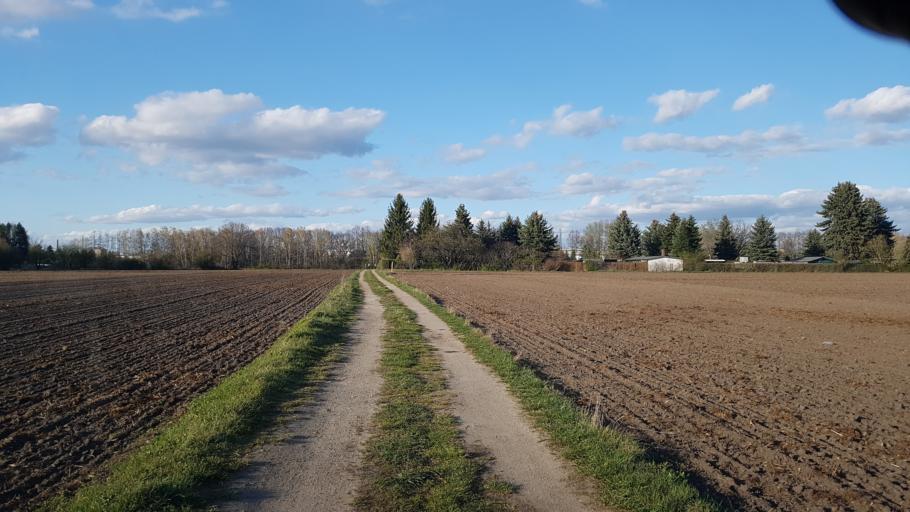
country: DE
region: Brandenburg
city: Finsterwalde
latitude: 51.6257
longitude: 13.7263
